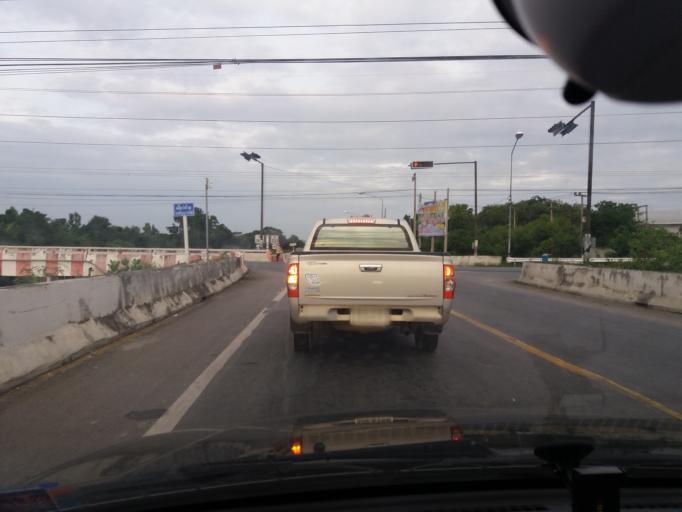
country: TH
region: Suphan Buri
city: U Thong
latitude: 14.5124
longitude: 99.9157
